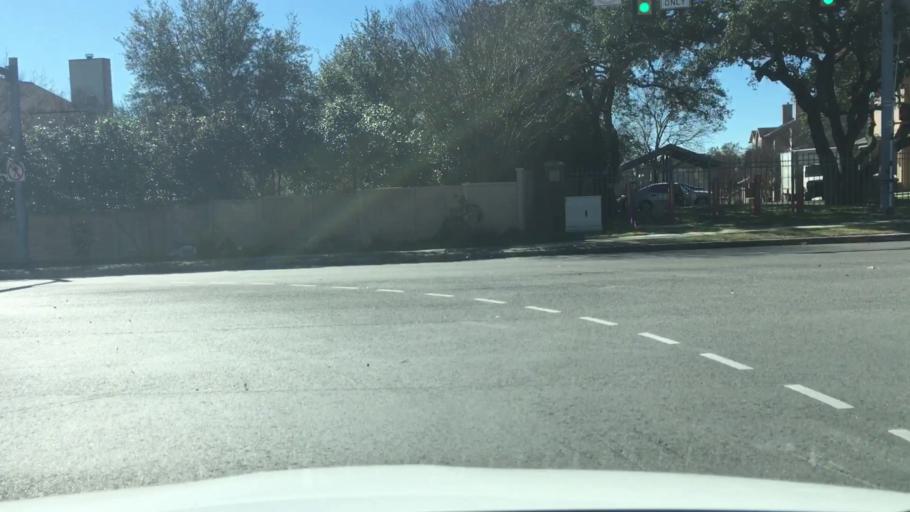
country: US
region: Texas
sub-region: Bexar County
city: Hollywood Park
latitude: 29.6024
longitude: -98.4593
